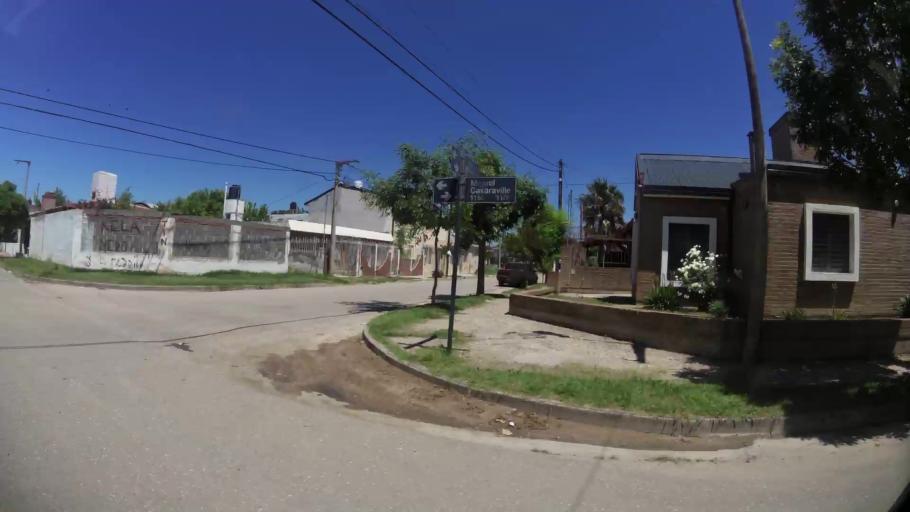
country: AR
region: Cordoba
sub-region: Departamento de Capital
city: Cordoba
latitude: -31.4184
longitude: -64.2351
